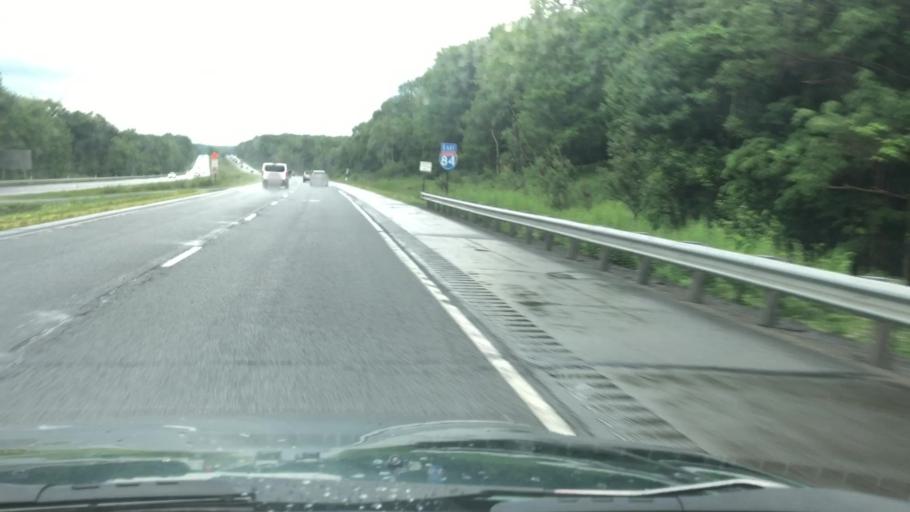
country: US
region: Pennsylvania
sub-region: Wayne County
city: Hawley
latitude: 41.3596
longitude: -75.1940
